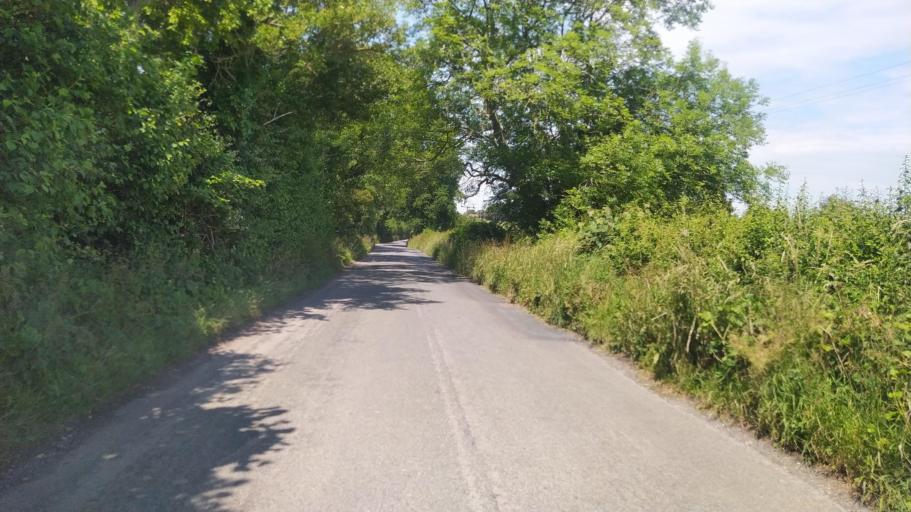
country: GB
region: England
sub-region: North Somerset
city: Banwell
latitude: 51.3337
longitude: -2.8890
